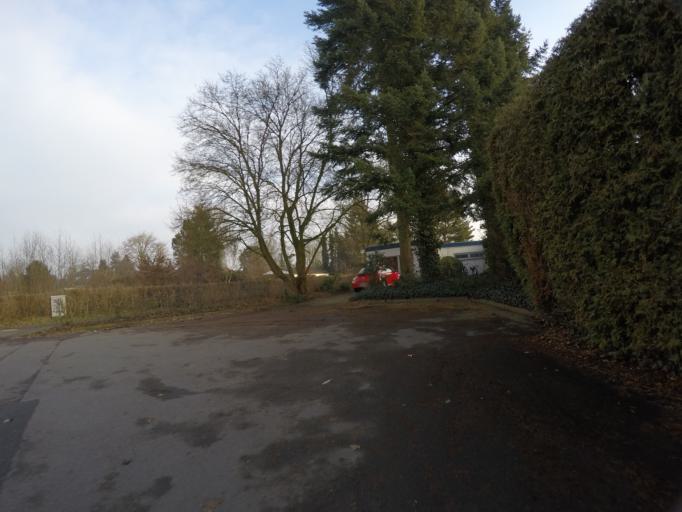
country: DE
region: Schleswig-Holstein
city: Quickborn
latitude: 53.7249
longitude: 9.9057
